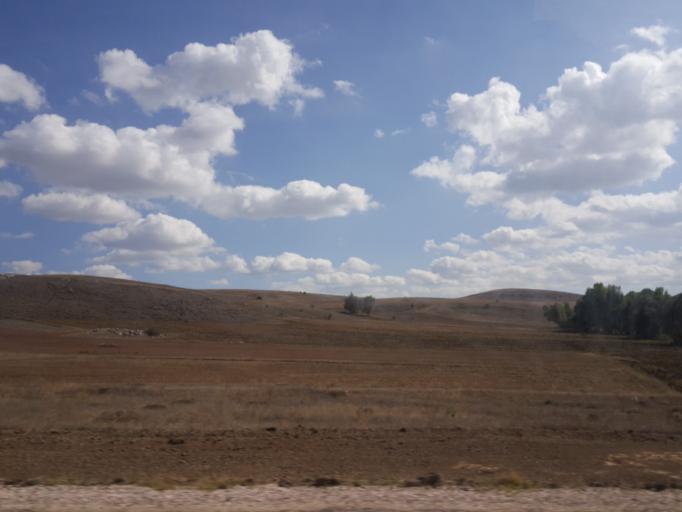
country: TR
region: Tokat
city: Artova
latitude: 40.1424
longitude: 36.3710
